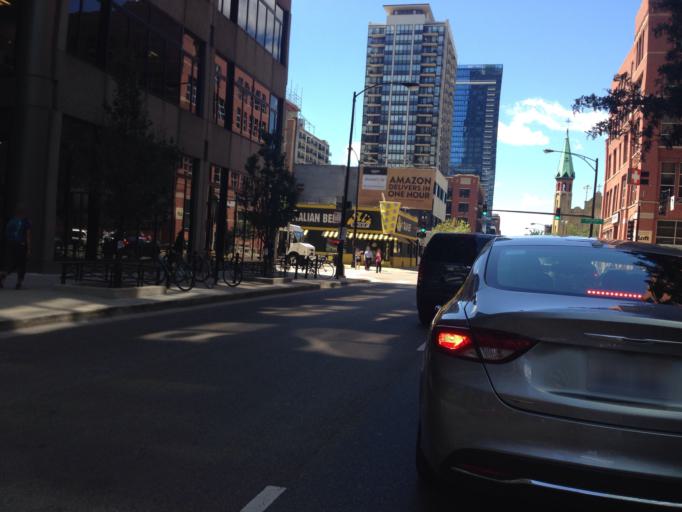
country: US
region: Illinois
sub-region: Cook County
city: Chicago
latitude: 41.8793
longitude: -87.6420
